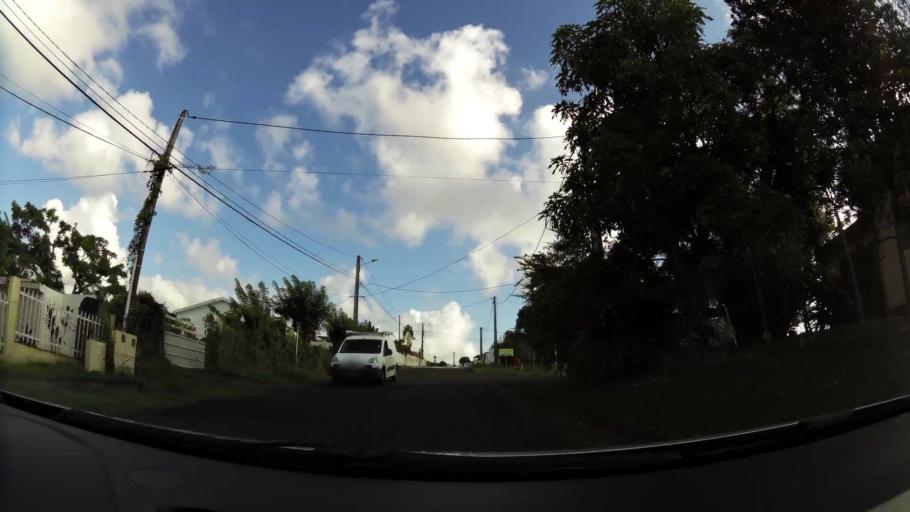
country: MQ
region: Martinique
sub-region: Martinique
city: Le Lamentin
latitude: 14.6232
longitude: -61.0155
